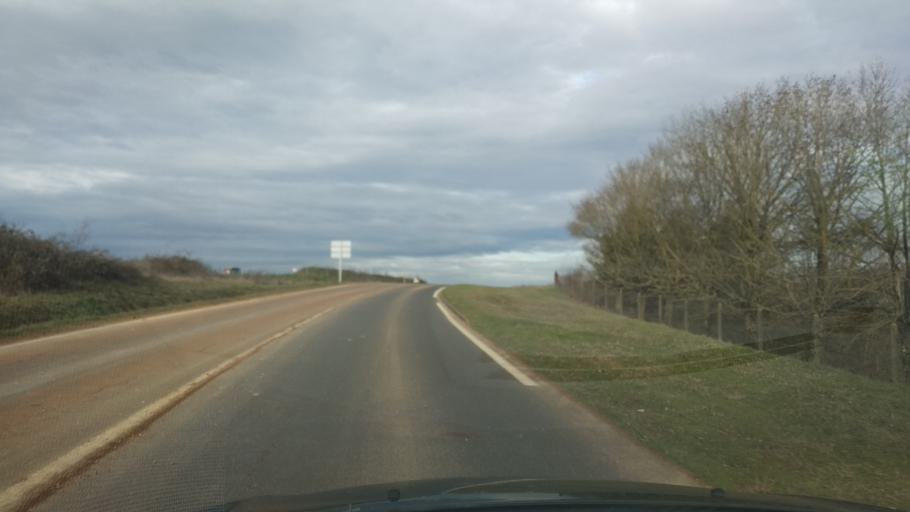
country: FR
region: Poitou-Charentes
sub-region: Departement de la Vienne
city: Saint-Georges-les-Baillargeaux
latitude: 46.6800
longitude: 0.4093
